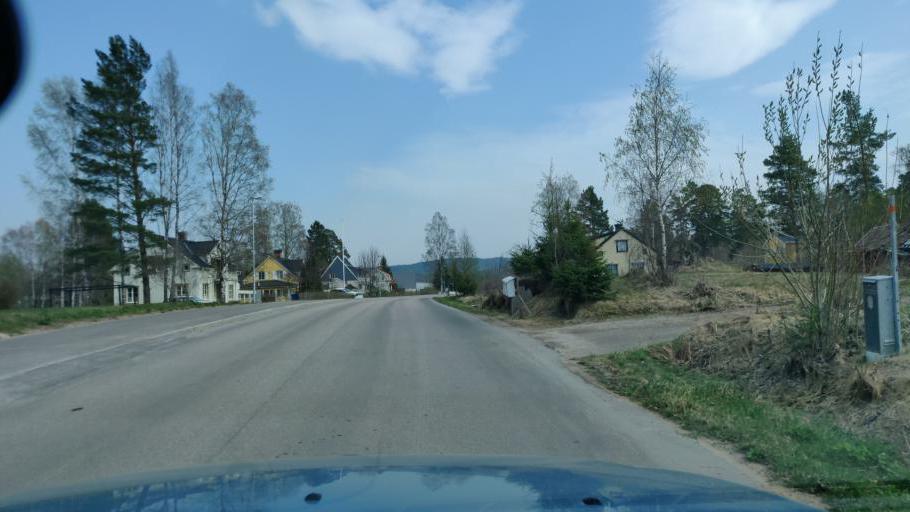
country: SE
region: Vaermland
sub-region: Munkfors Kommun
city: Munkfors
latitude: 59.8406
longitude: 13.5578
